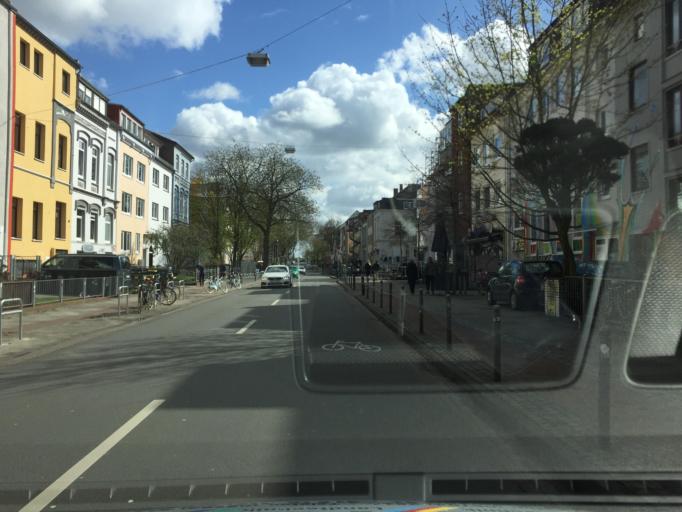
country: DE
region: Bremen
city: Bremen
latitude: 53.0720
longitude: 8.8235
